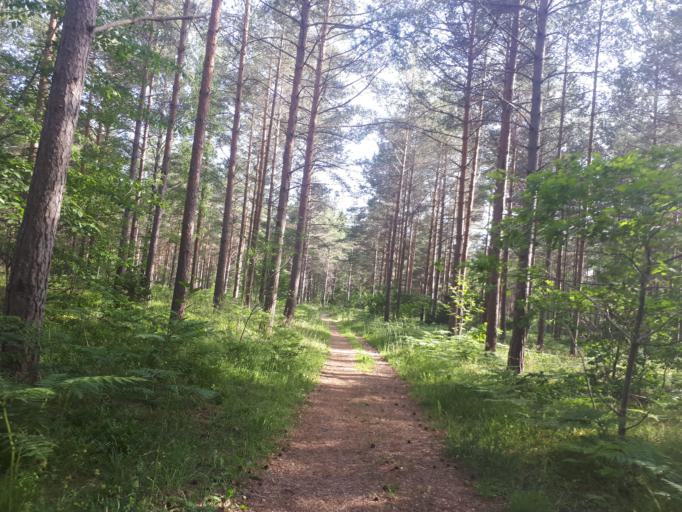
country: SE
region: Gotland
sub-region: Gotland
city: Visby
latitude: 57.6095
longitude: 18.2925
